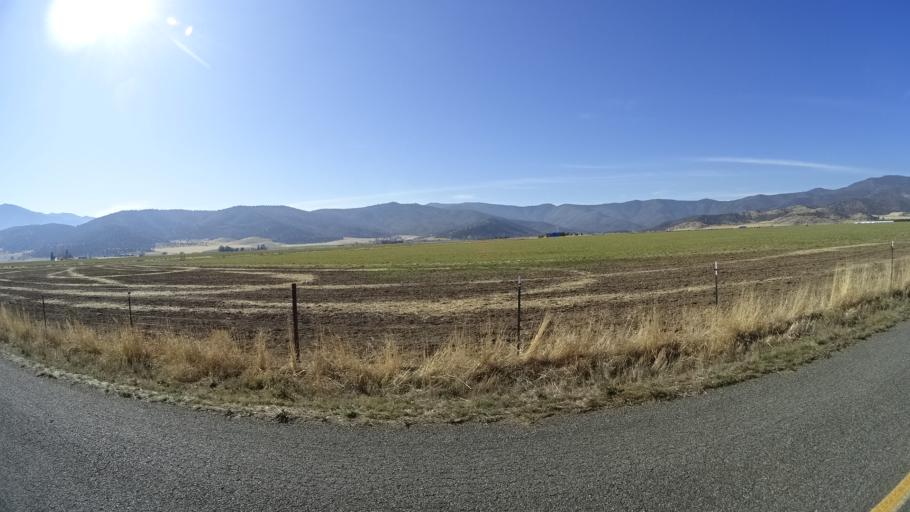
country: US
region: California
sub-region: Siskiyou County
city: Montague
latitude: 41.5468
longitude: -122.5410
